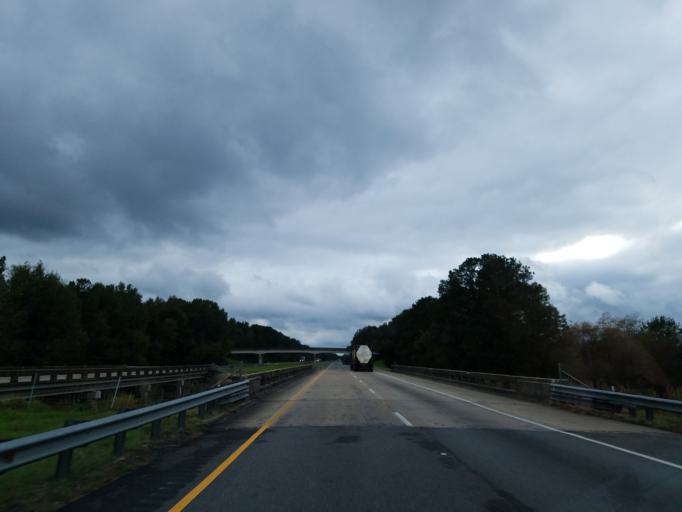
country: US
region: Alabama
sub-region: Greene County
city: Eutaw
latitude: 32.7627
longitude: -88.0693
